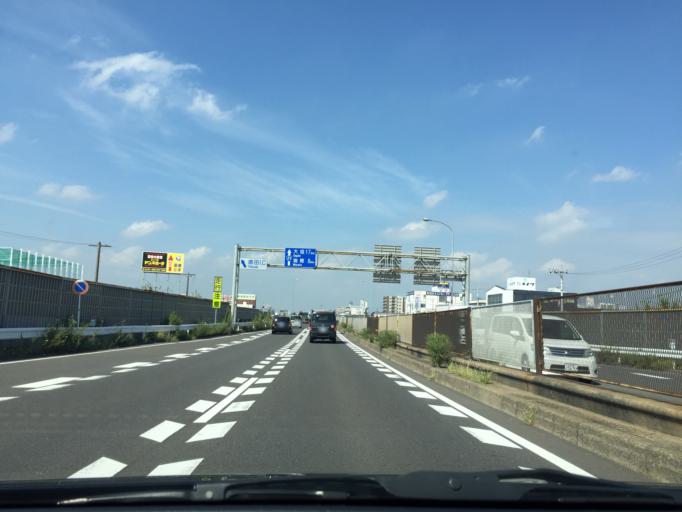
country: JP
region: Gifu
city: Kasamatsucho
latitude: 35.3884
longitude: 136.7757
